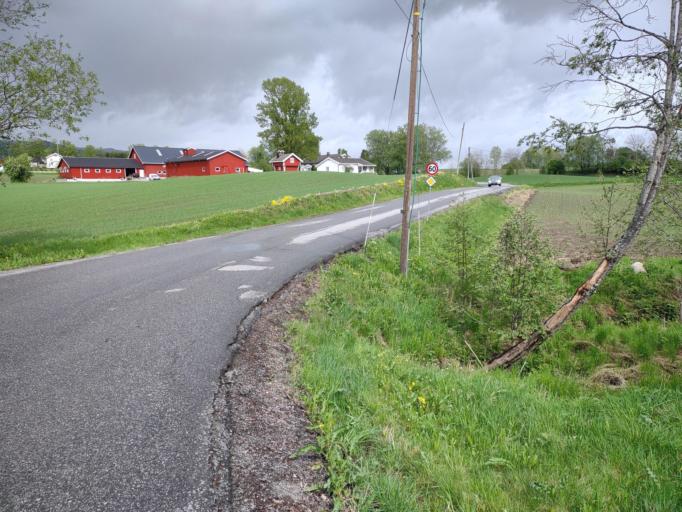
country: NO
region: Akershus
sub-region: Nannestad
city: Teigebyen
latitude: 60.2446
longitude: 10.9898
